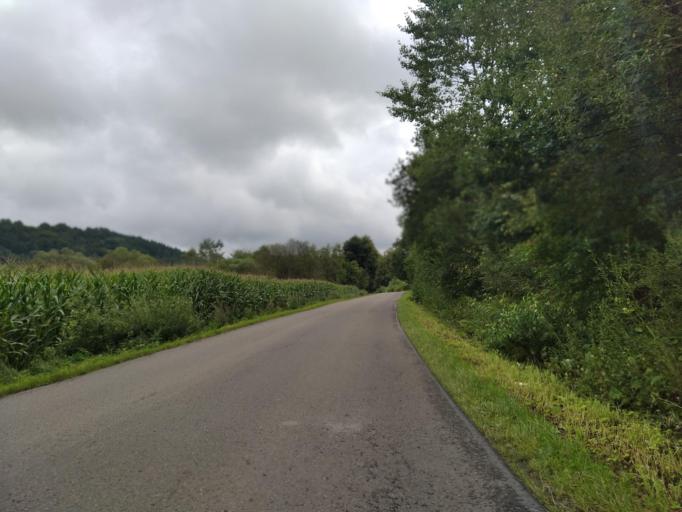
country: PL
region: Subcarpathian Voivodeship
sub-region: Powiat brzozowski
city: Nozdrzec
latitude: 49.7368
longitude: 22.2533
